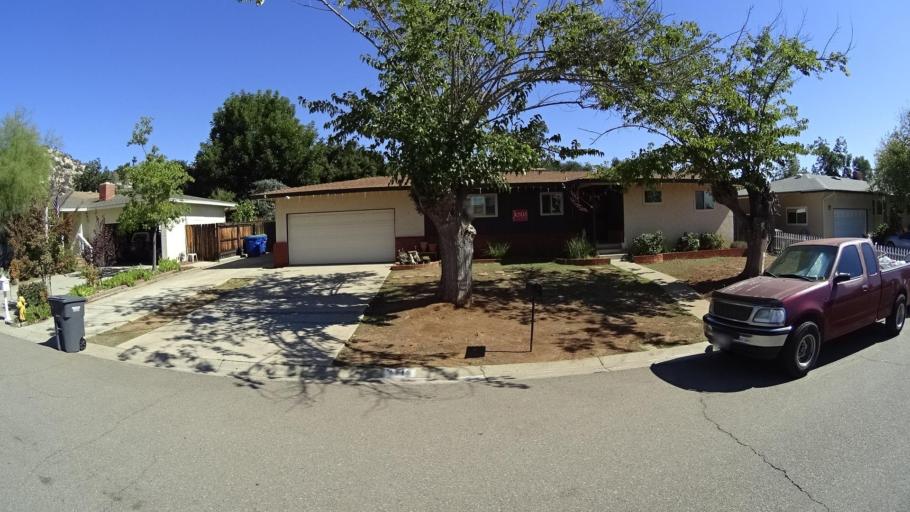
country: US
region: California
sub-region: San Diego County
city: Santee
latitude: 32.8269
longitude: -116.9576
